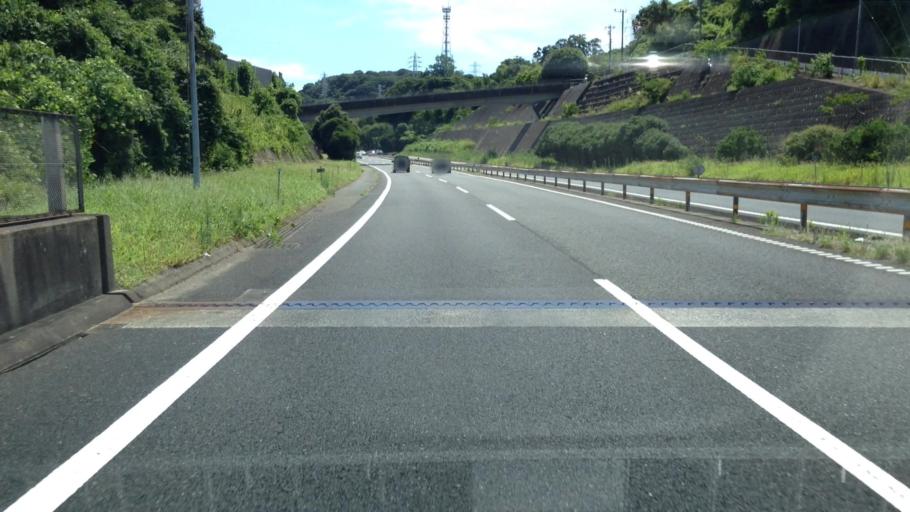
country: JP
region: Kanagawa
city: Yokosuka
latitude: 35.2629
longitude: 139.6326
